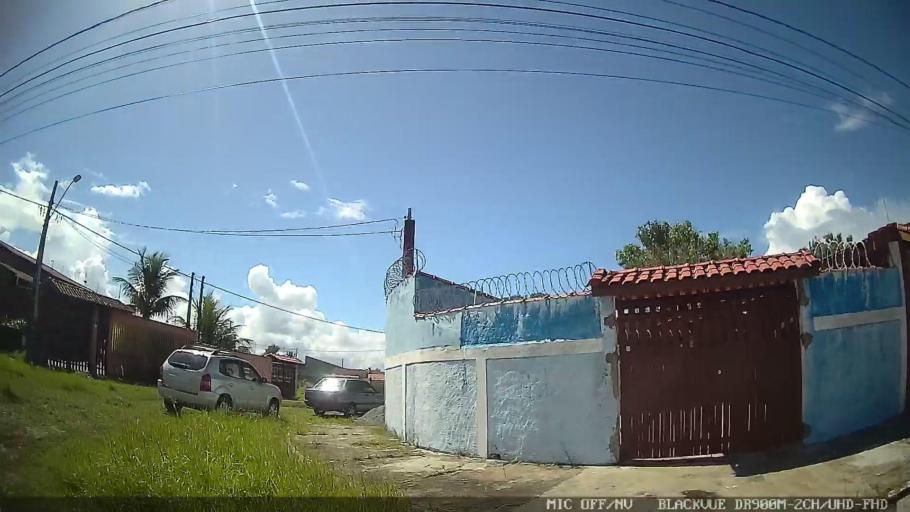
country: BR
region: Sao Paulo
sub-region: Itanhaem
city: Itanhaem
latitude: -24.2311
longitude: -46.8783
